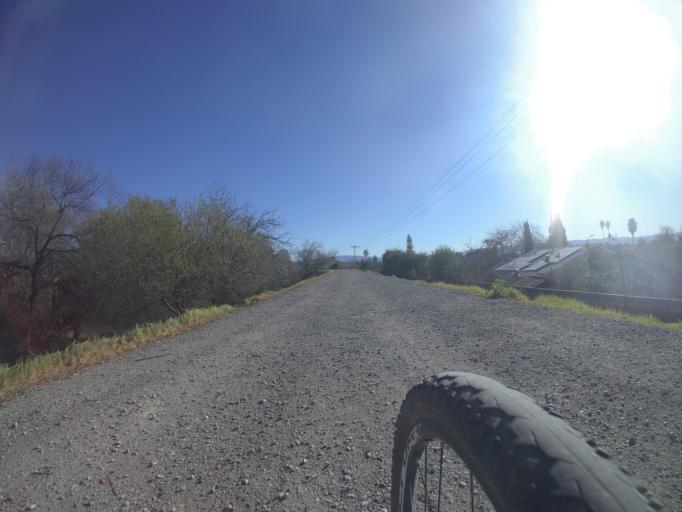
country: US
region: California
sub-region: Santa Clara County
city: Santa Clara
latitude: 37.3919
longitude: -121.9402
